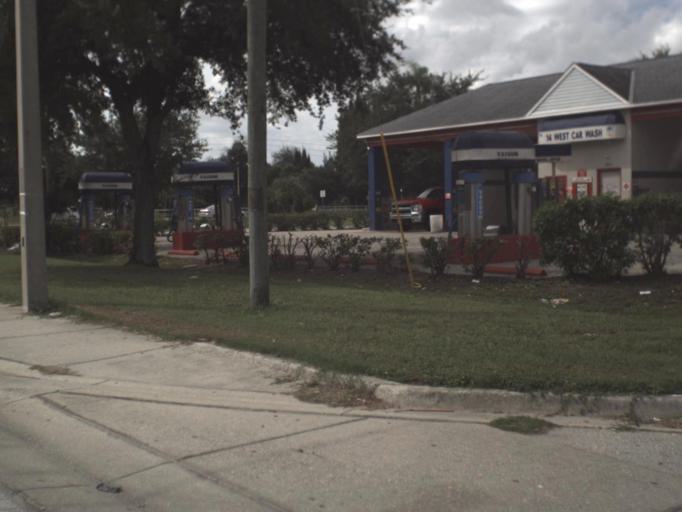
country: US
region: Florida
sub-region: Manatee County
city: South Bradenton
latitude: 27.4747
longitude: -82.5755
